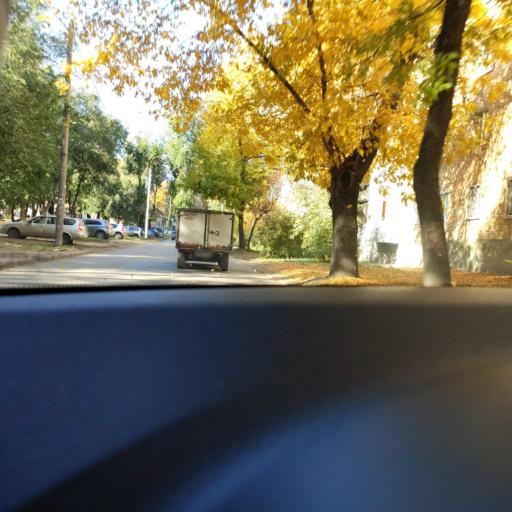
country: RU
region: Samara
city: Samara
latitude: 53.2256
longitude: 50.2442
